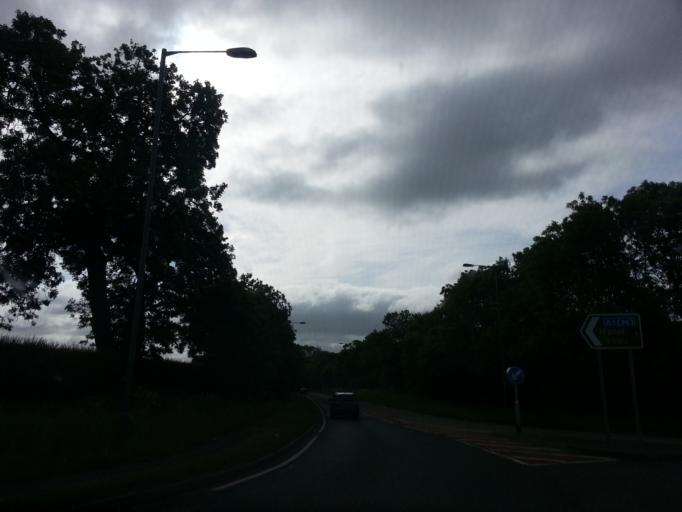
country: GB
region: England
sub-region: County Durham
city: Spennymoor
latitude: 54.6579
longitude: -1.6096
